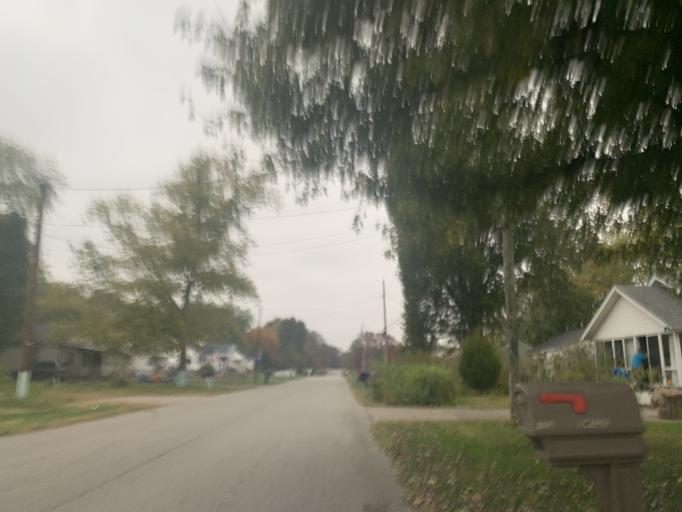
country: US
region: Kentucky
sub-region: Jefferson County
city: Saint Dennis
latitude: 38.2060
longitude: -85.8540
